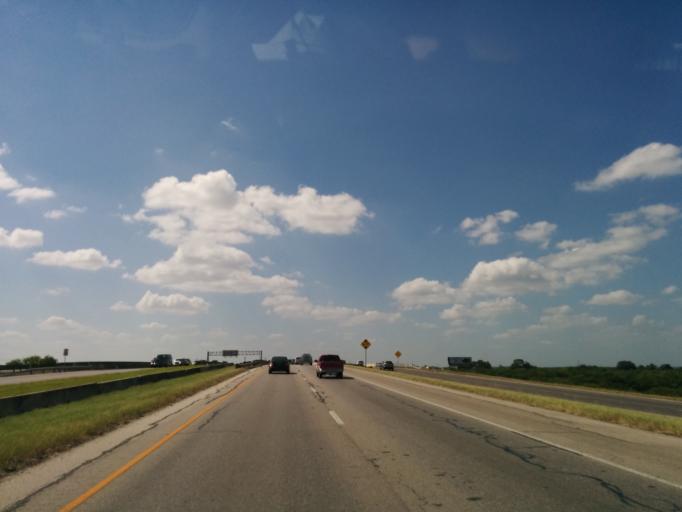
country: US
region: Texas
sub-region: Bexar County
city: Live Oak
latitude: 29.5801
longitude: -98.3437
